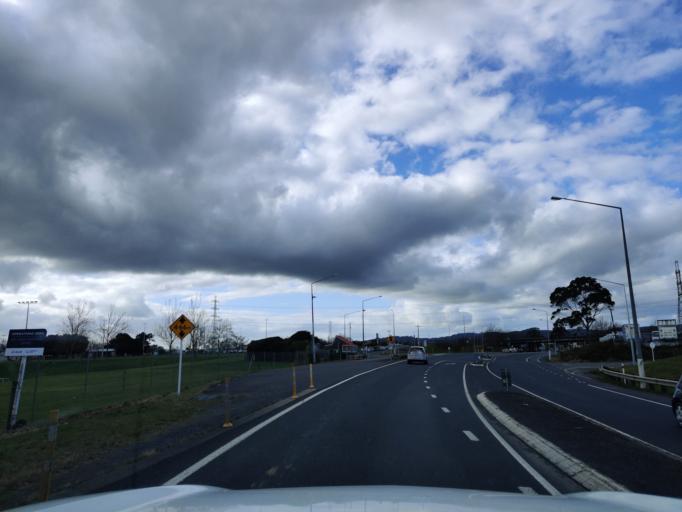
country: NZ
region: Auckland
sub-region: Auckland
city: Papakura
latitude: -37.1091
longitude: 174.9436
